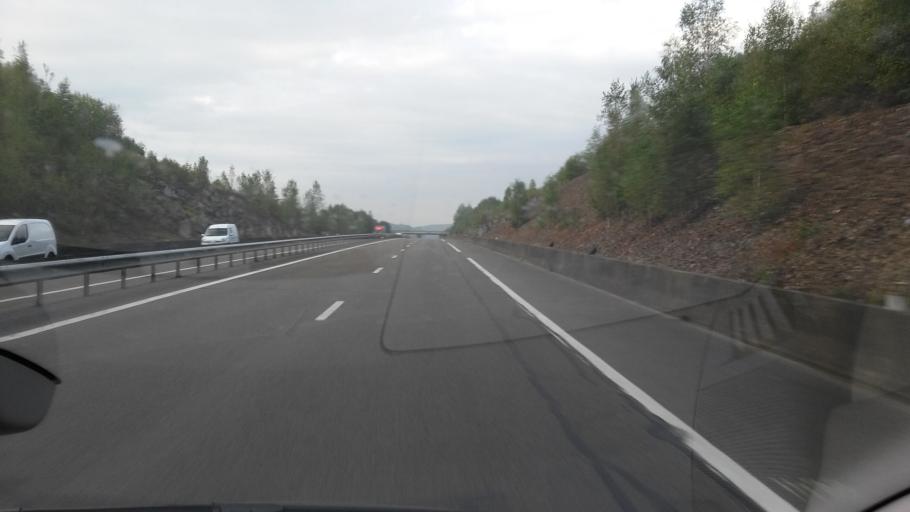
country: FR
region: Champagne-Ardenne
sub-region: Departement des Ardennes
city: Attigny
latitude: 49.6299
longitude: 4.5568
